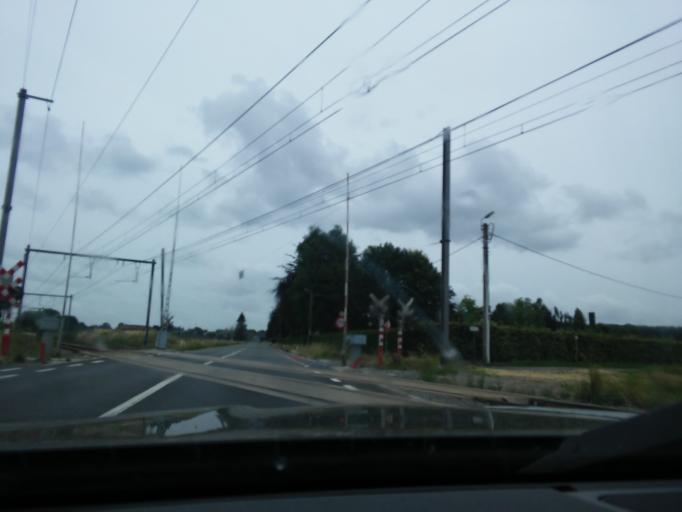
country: BE
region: Flanders
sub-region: Provincie Vlaams-Brabant
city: Herne
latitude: 50.7106
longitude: 4.0281
